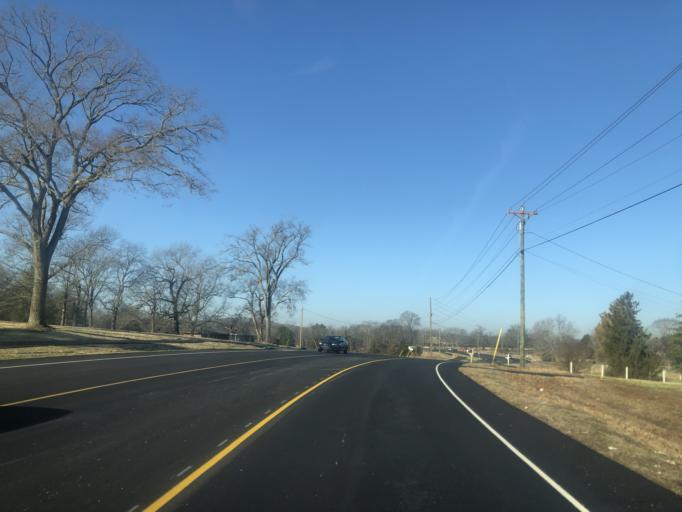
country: US
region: Tennessee
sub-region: Williamson County
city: Nolensville
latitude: 35.9594
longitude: -86.6774
